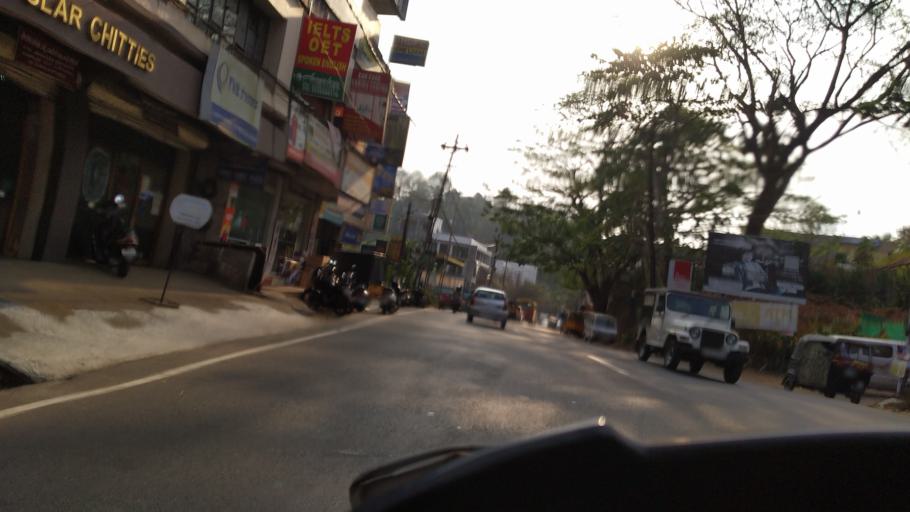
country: IN
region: Kerala
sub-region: Kottayam
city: Erattupetta
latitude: 9.5556
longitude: 76.7920
